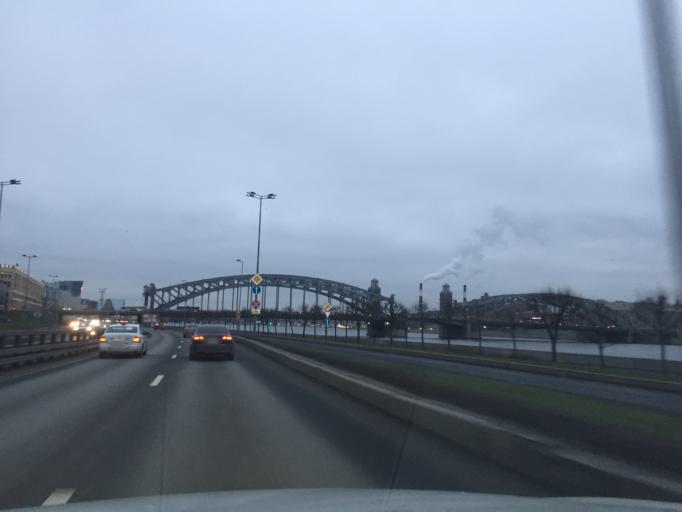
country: RU
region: St.-Petersburg
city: Centralniy
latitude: 59.9453
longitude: 30.4054
